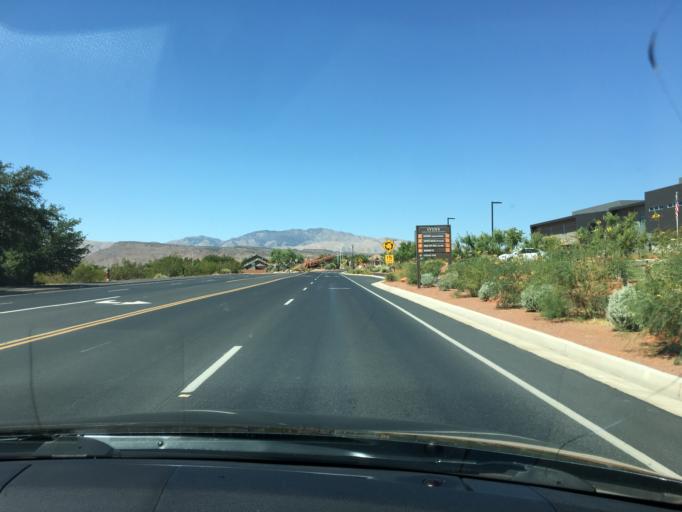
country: US
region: Utah
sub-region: Washington County
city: Ivins
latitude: 37.1685
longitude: -113.6729
